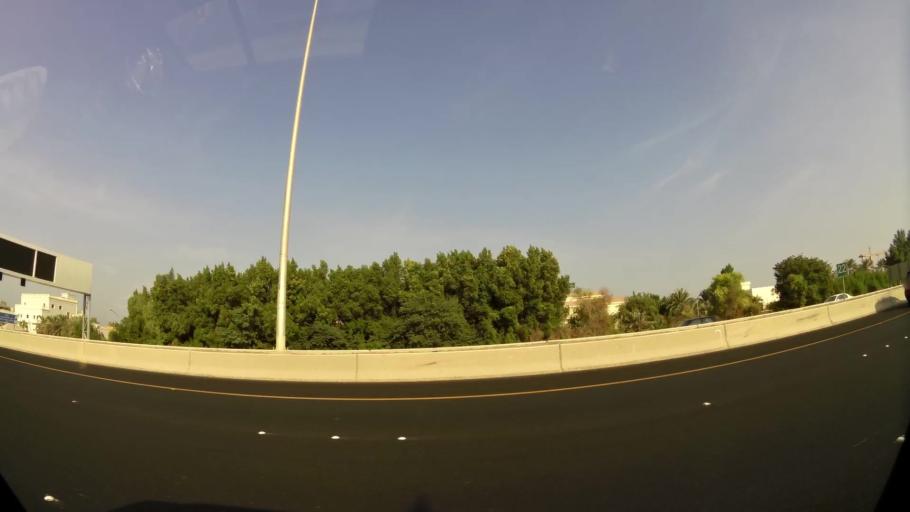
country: KW
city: Al Funaytis
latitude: 29.2049
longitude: 48.1055
